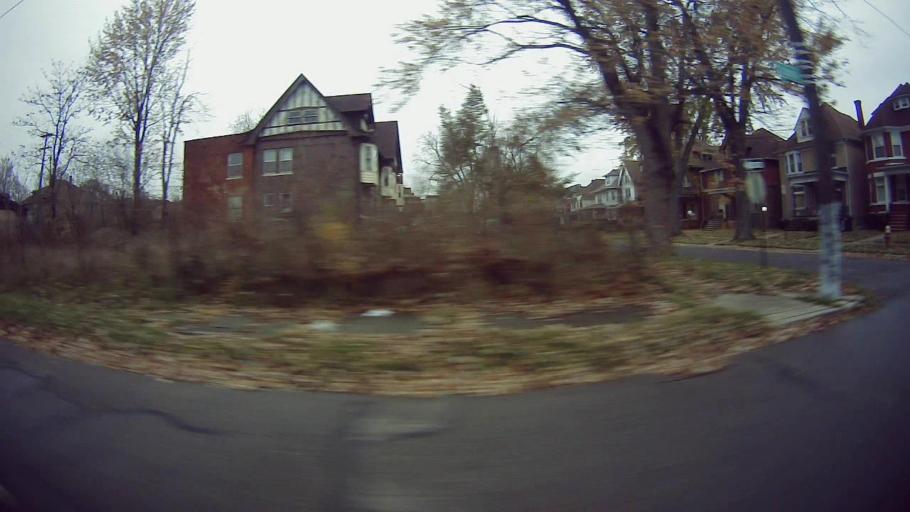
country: US
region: Michigan
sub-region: Wayne County
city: Hamtramck
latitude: 42.3795
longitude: -83.0768
